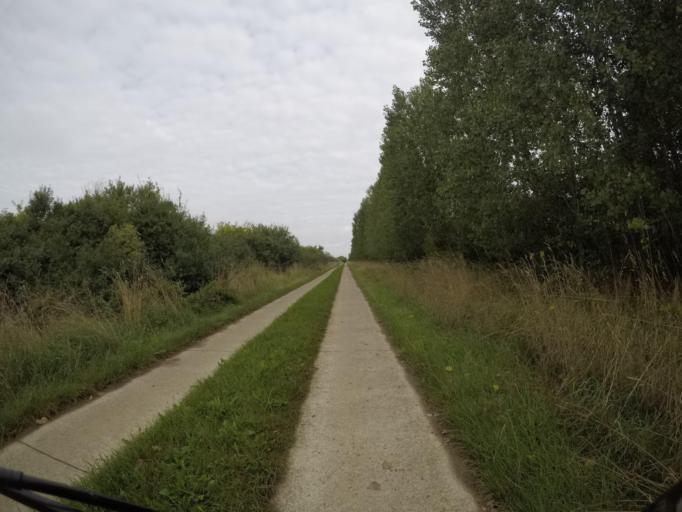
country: DE
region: Lower Saxony
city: Neu Darchau
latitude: 53.3071
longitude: 10.8728
